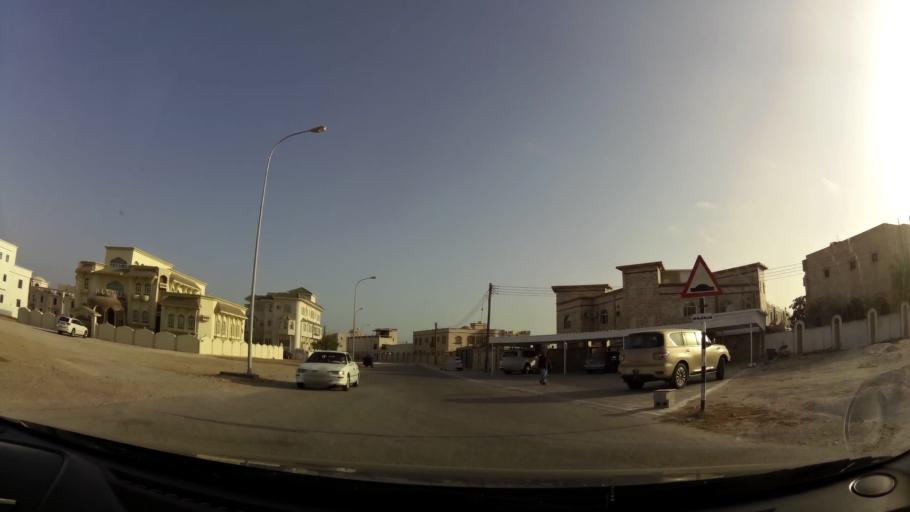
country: OM
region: Zufar
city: Salalah
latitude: 17.0025
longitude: 54.0281
